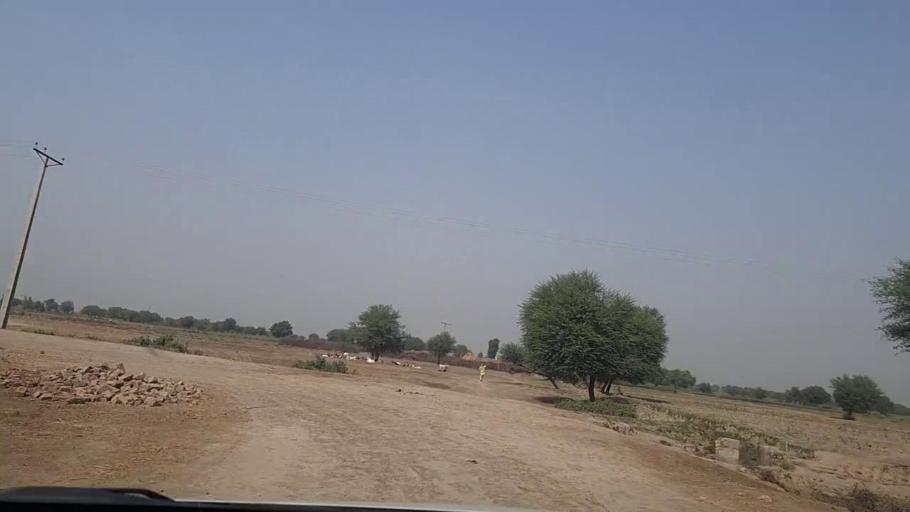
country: PK
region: Sindh
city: Mirpur Khas
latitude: 25.6208
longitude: 69.2009
